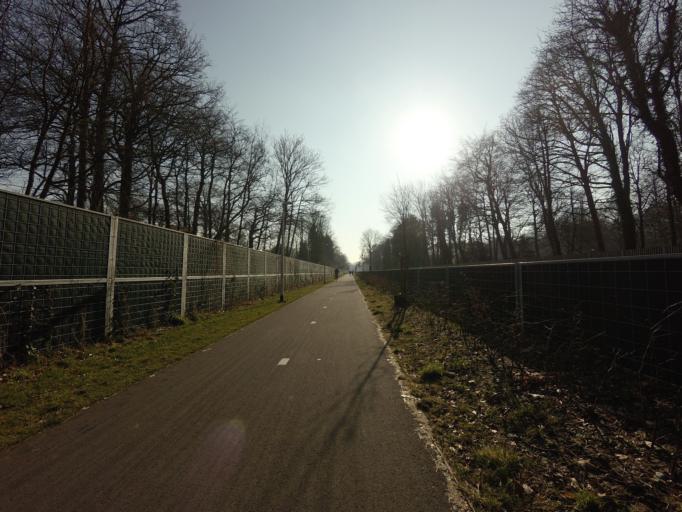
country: NL
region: North Holland
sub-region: Gemeente Velsen
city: Velsen-Zuid
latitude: 52.4469
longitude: 4.6328
